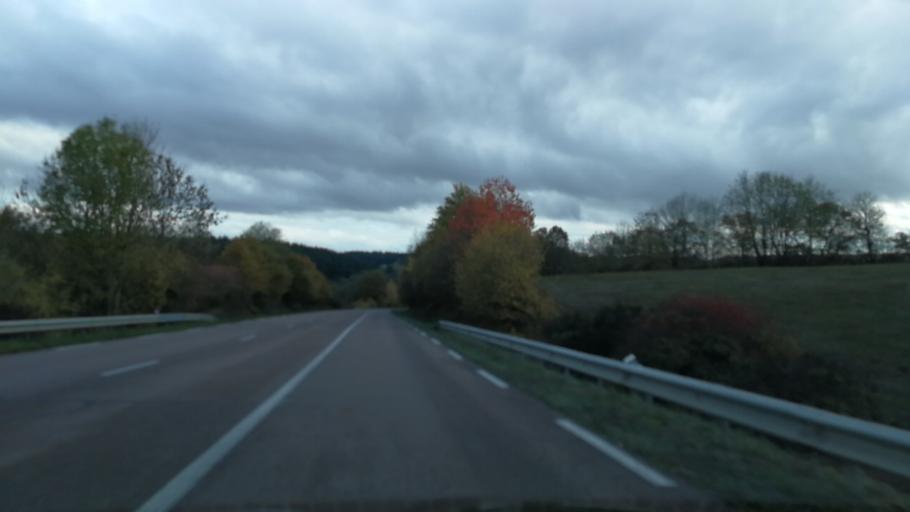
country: FR
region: Bourgogne
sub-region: Departement de la Cote-d'Or
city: Saulieu
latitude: 47.2623
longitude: 4.2637
